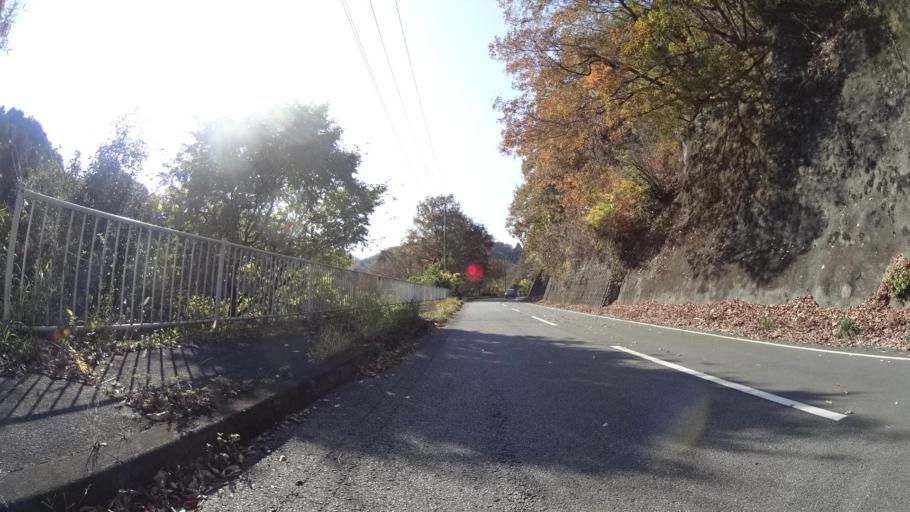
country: JP
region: Yamanashi
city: Uenohara
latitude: 35.5892
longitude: 139.1672
